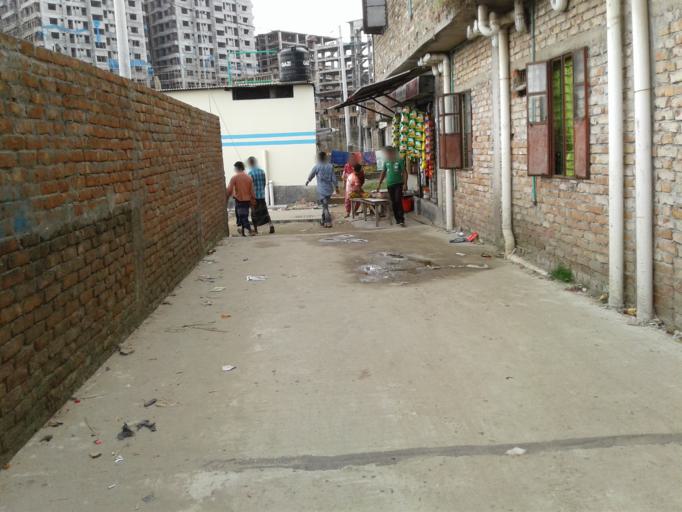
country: BD
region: Dhaka
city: Azimpur
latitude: 23.8104
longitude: 90.3816
